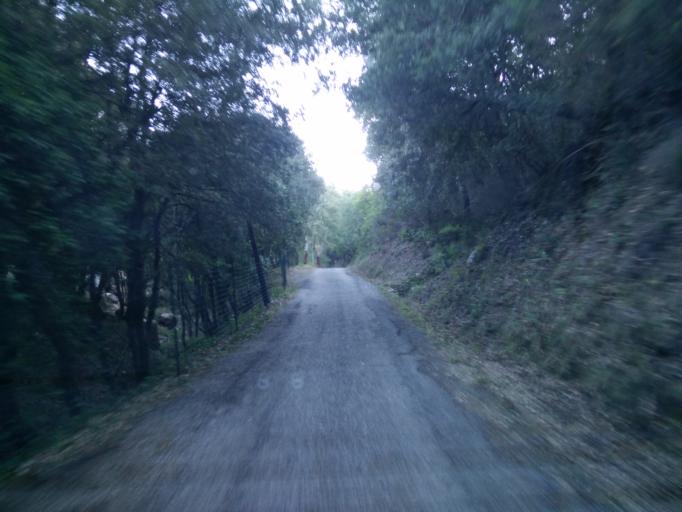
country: FR
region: Provence-Alpes-Cote d'Azur
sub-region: Departement du Var
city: Collobrieres
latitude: 43.2586
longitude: 6.3050
